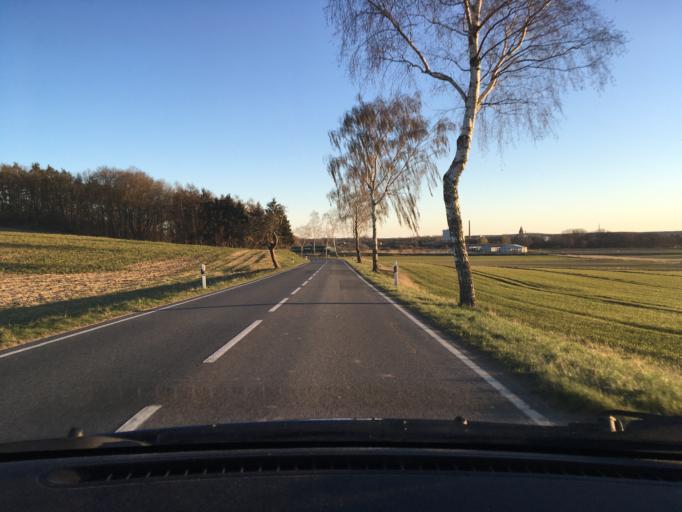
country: DE
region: Lower Saxony
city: Dahlem
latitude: 53.1995
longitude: 10.7511
